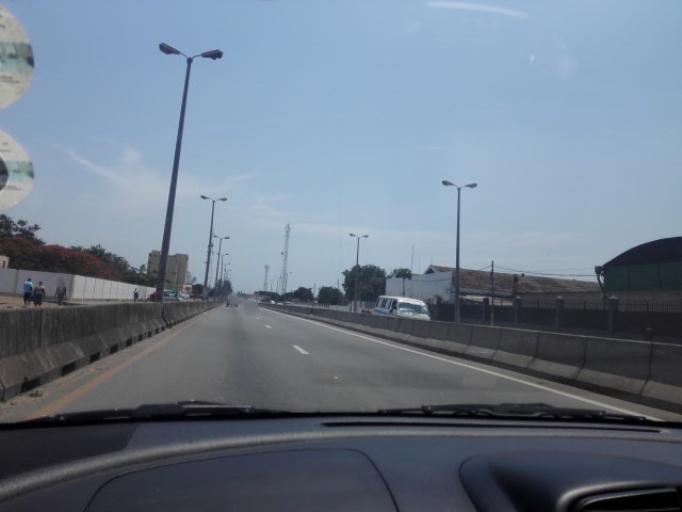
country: MZ
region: Maputo City
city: Maputo
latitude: -25.9391
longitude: 32.5461
